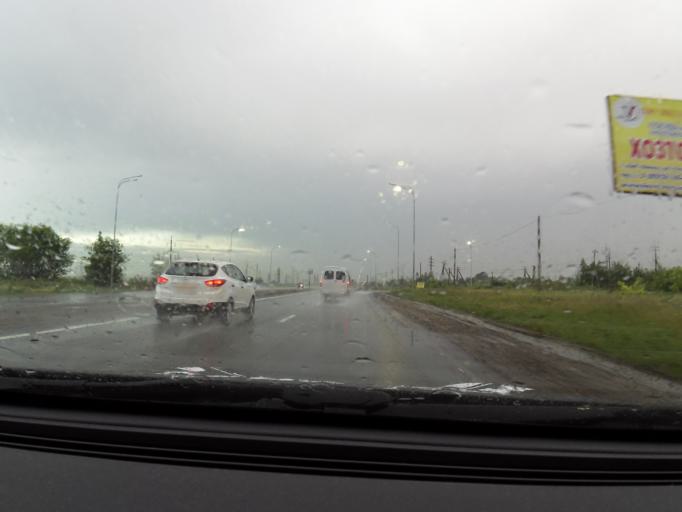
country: RU
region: Tatarstan
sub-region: Tukayevskiy Rayon
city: Naberezhnyye Chelny
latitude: 55.6834
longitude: 52.4802
